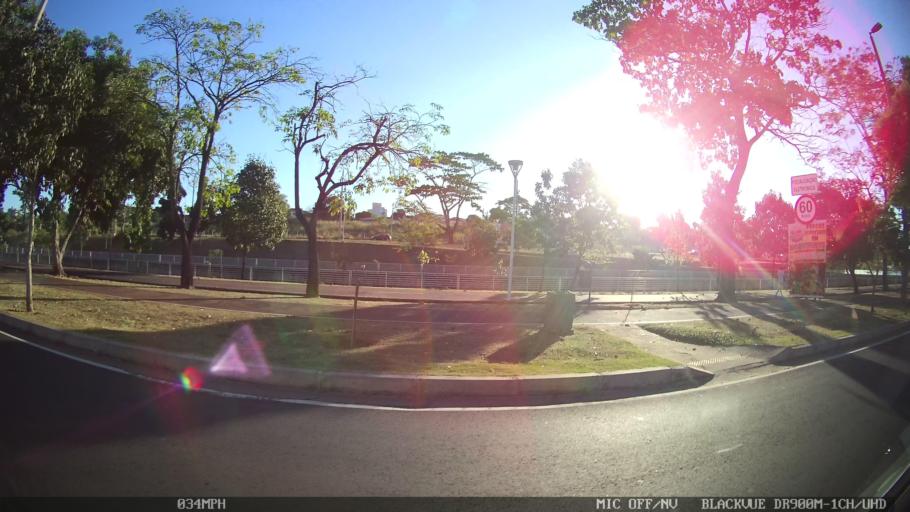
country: BR
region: Sao Paulo
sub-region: Sao Jose Do Rio Preto
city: Sao Jose do Rio Preto
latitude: -20.7933
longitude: -49.3762
